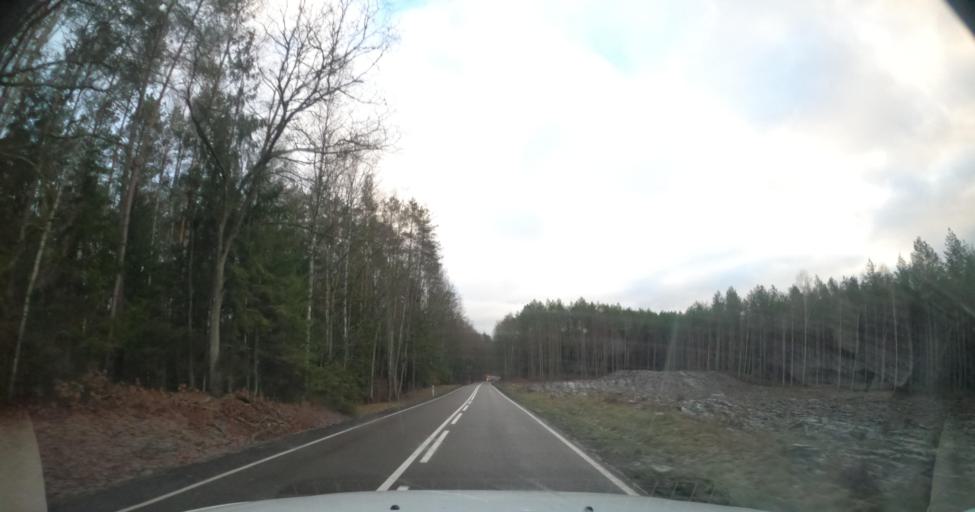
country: PL
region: West Pomeranian Voivodeship
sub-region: Powiat drawski
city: Zlocieniec
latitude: 53.5347
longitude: 16.0844
